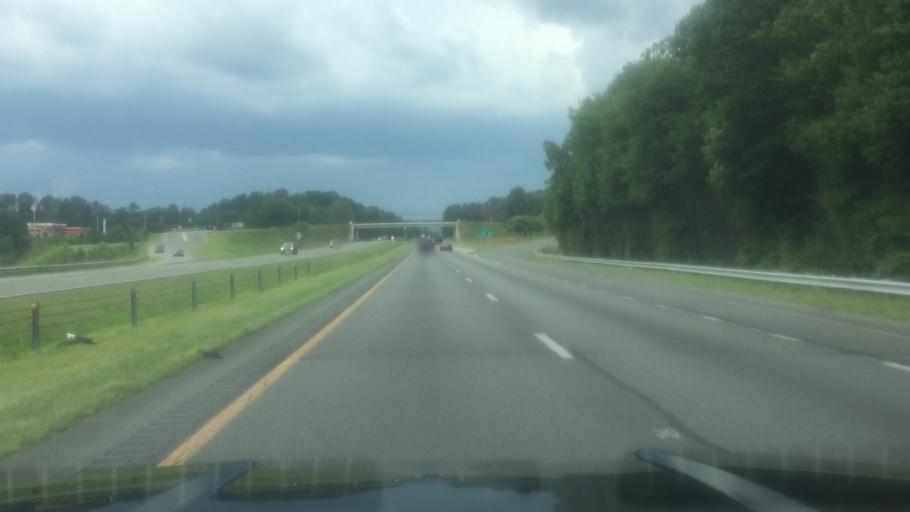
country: US
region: North Carolina
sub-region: Surry County
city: Pilot Mountain
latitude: 36.3728
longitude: -80.4851
